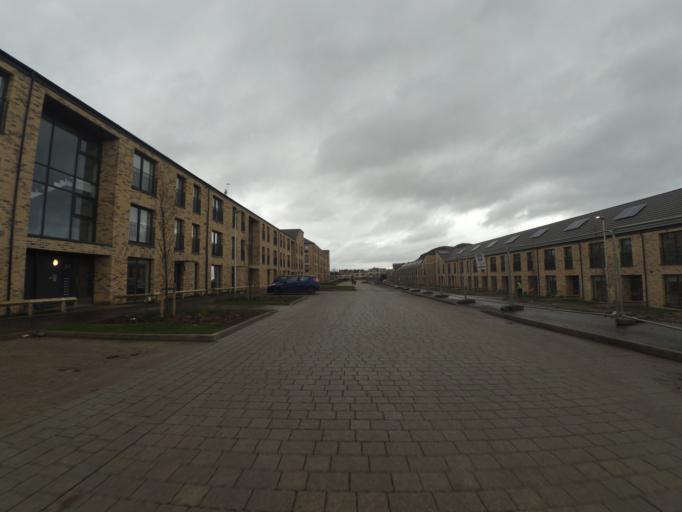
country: GB
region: Scotland
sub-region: West Lothian
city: Seafield
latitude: 55.9339
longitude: -3.1321
